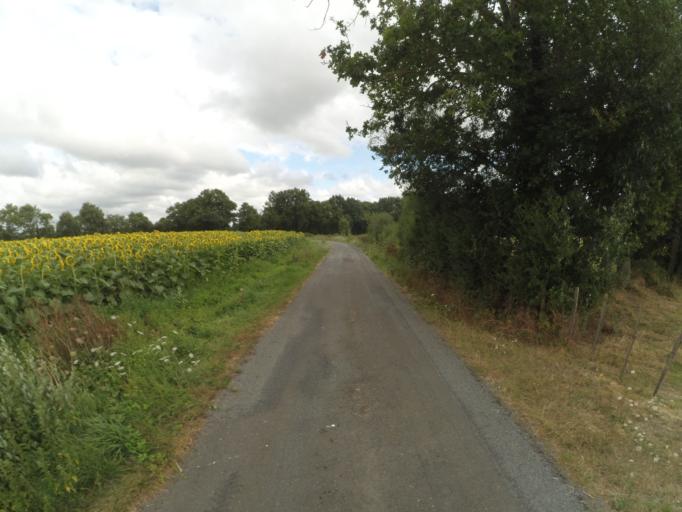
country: FR
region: Pays de la Loire
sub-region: Departement de la Vendee
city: Saint-Philbert-de-Bouaine
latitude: 46.9891
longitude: -1.4851
